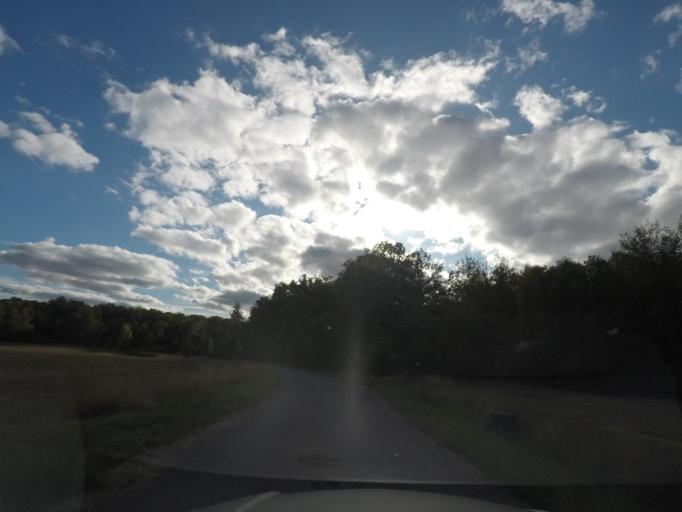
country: SE
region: Vaestmanland
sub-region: Hallstahammars Kommun
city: Kolback
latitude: 59.4857
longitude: 16.1818
